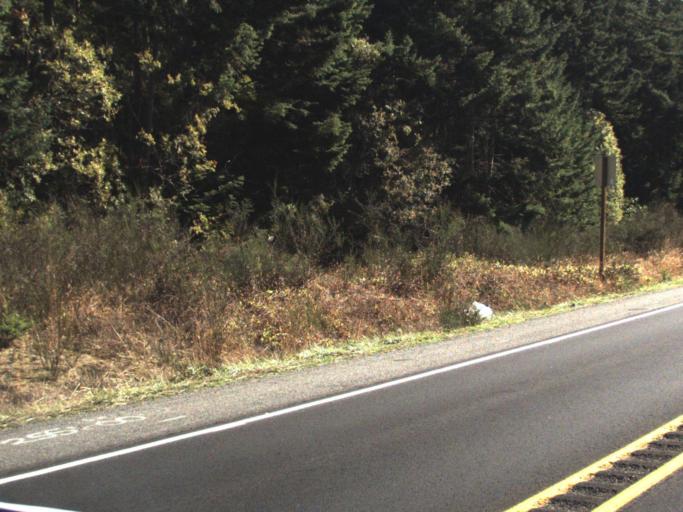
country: US
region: Washington
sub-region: Island County
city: Coupeville
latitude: 48.2294
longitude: -122.7399
